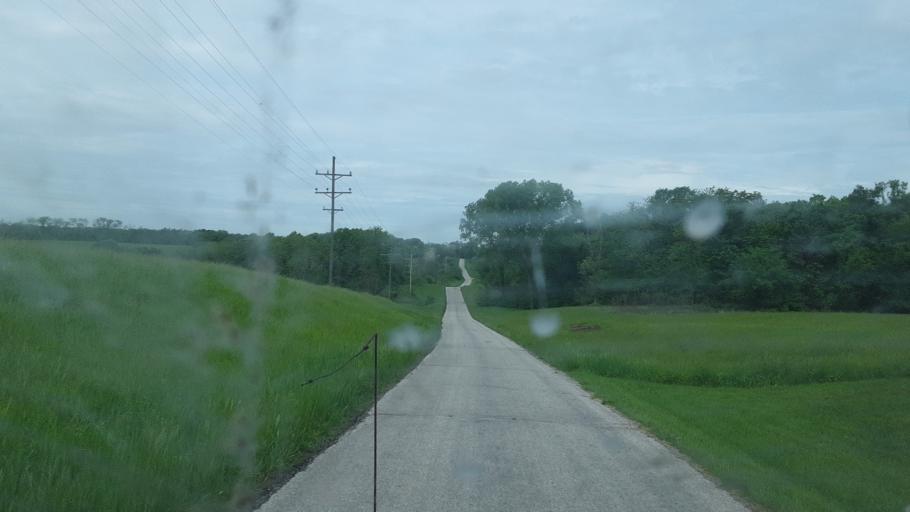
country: US
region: Missouri
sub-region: Clark County
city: Kahoka
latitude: 40.4237
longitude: -91.5968
